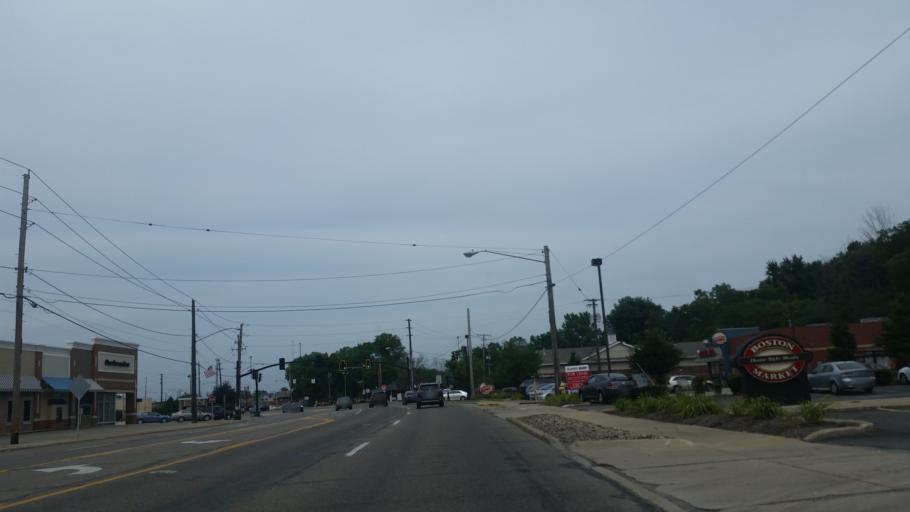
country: US
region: Ohio
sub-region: Cuyahoga County
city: Solon
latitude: 41.3841
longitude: -81.4340
